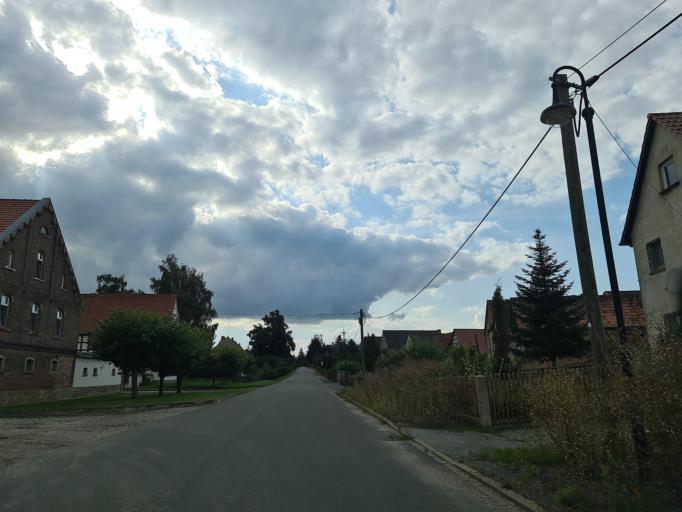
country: DE
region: Thuringia
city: Walpernhain
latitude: 51.0299
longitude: 11.9692
